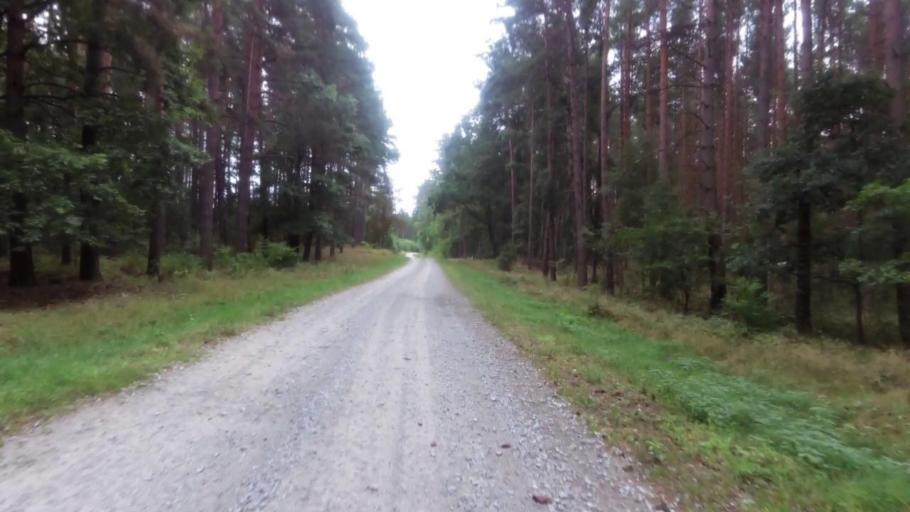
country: PL
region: Lubusz
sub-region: Powiat gorzowski
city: Kostrzyn nad Odra
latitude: 52.6479
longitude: 14.6407
